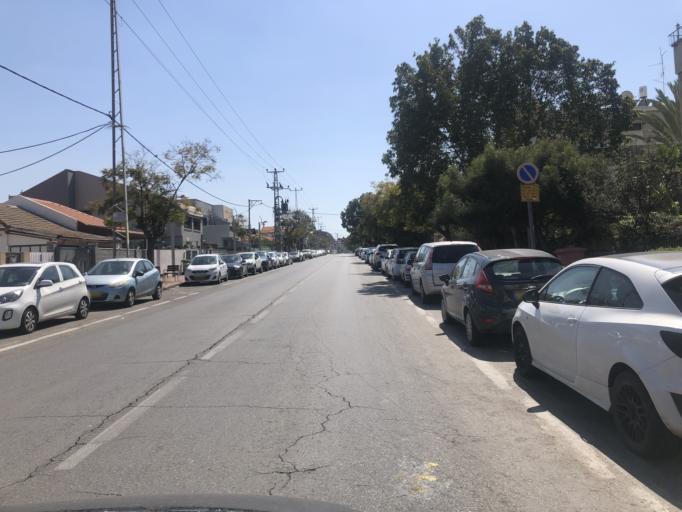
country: IL
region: Tel Aviv
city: Holon
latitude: 32.0095
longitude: 34.7648
